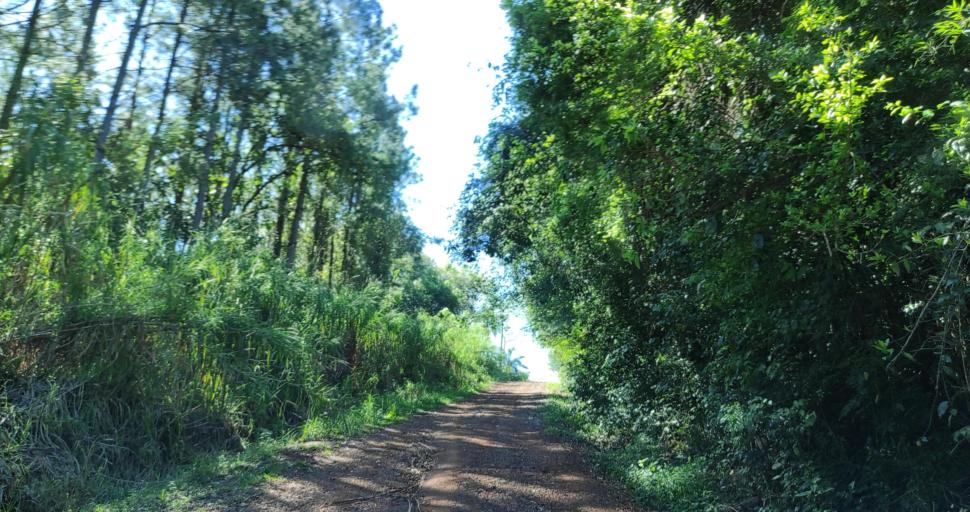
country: AR
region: Misiones
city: Capiovi
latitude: -26.9437
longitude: -55.0026
